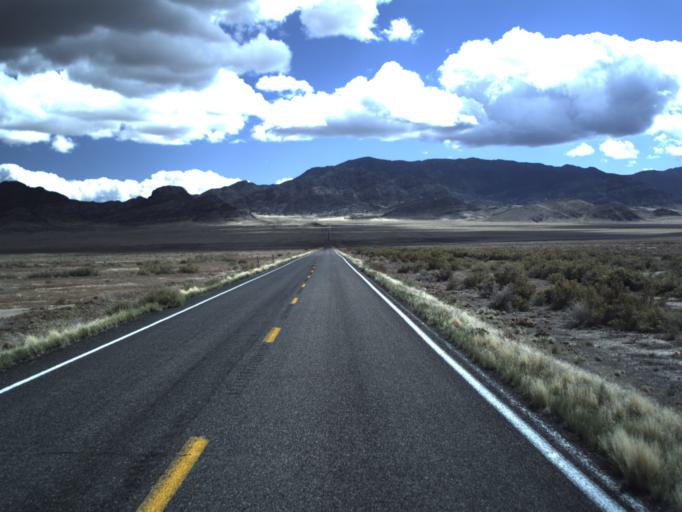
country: US
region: Utah
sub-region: Beaver County
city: Milford
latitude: 38.5260
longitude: -113.6648
